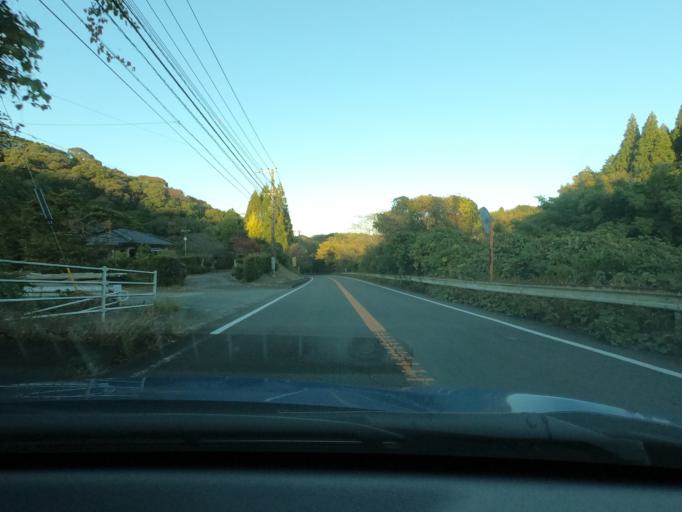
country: JP
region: Kagoshima
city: Satsumasendai
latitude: 31.8104
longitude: 130.3699
